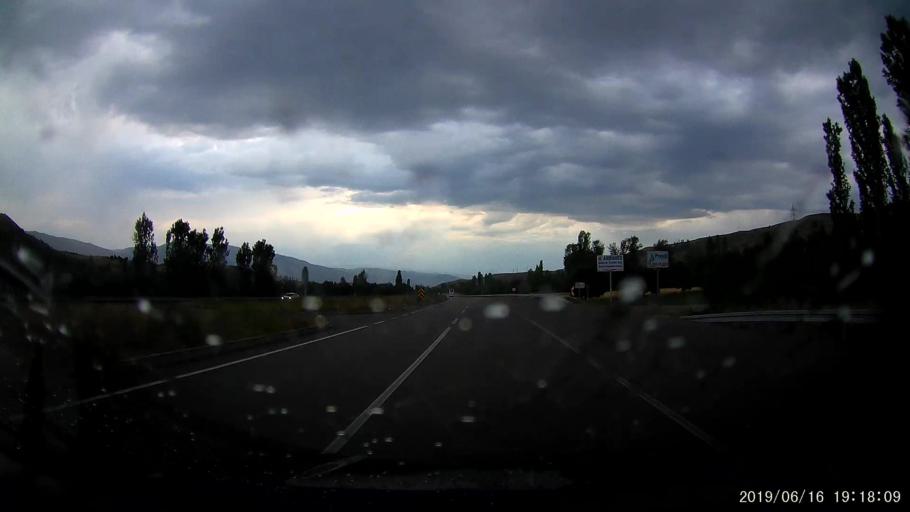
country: TR
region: Sivas
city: Akincilar
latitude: 40.0948
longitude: 38.4659
